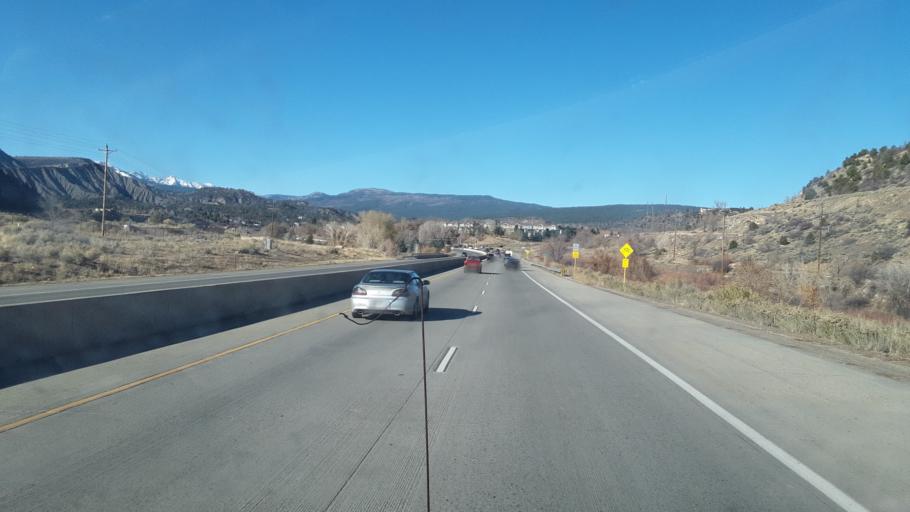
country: US
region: Colorado
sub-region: La Plata County
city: Durango
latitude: 37.2567
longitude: -107.8761
